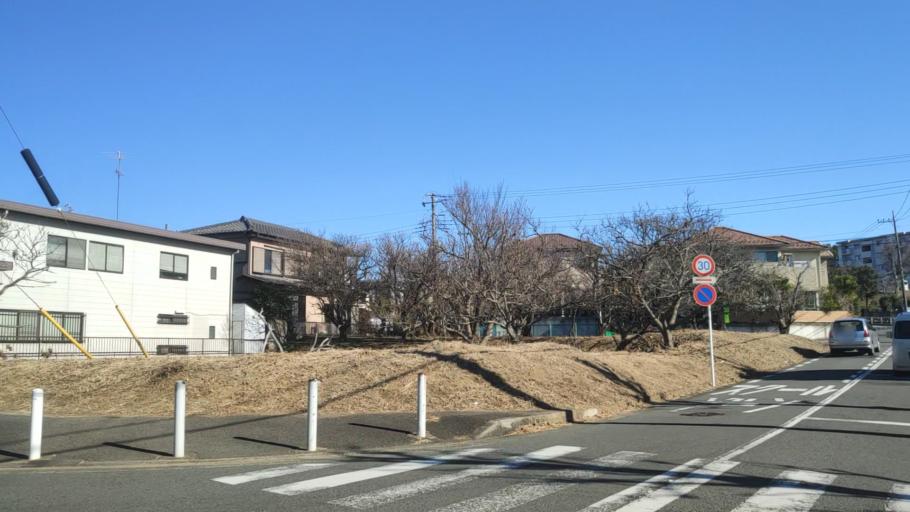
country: JP
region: Tokyo
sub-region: Machida-shi
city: Machida
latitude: 35.5144
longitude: 139.5072
